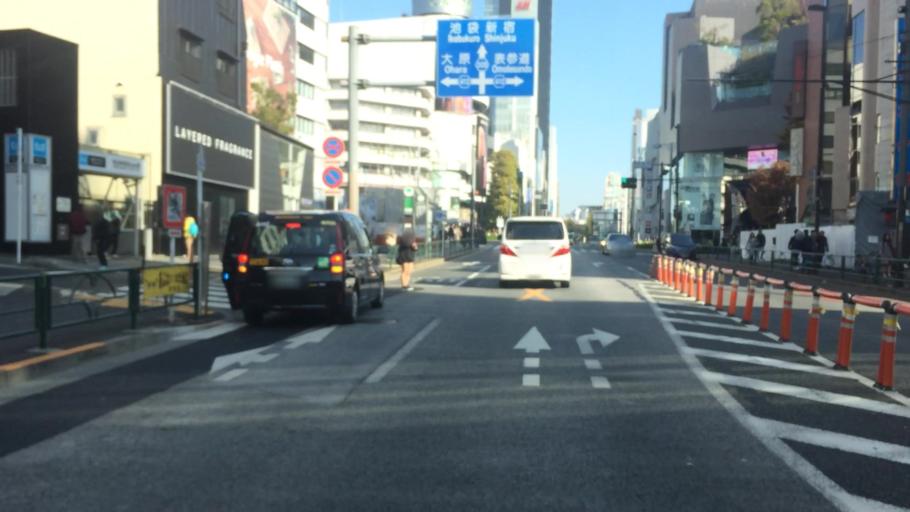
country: JP
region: Tokyo
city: Tokyo
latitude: 35.6677
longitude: 139.7048
